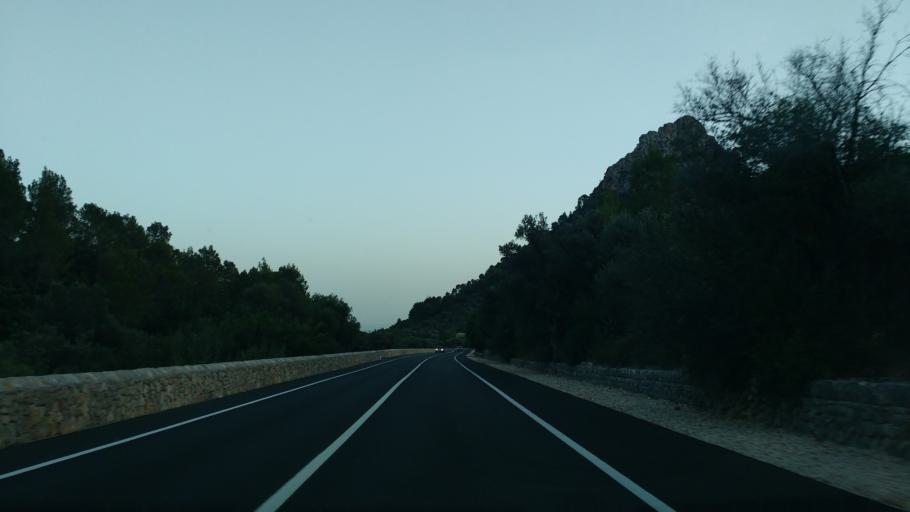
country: ES
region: Balearic Islands
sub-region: Illes Balears
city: Bunyola
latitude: 39.7112
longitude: 2.6895
